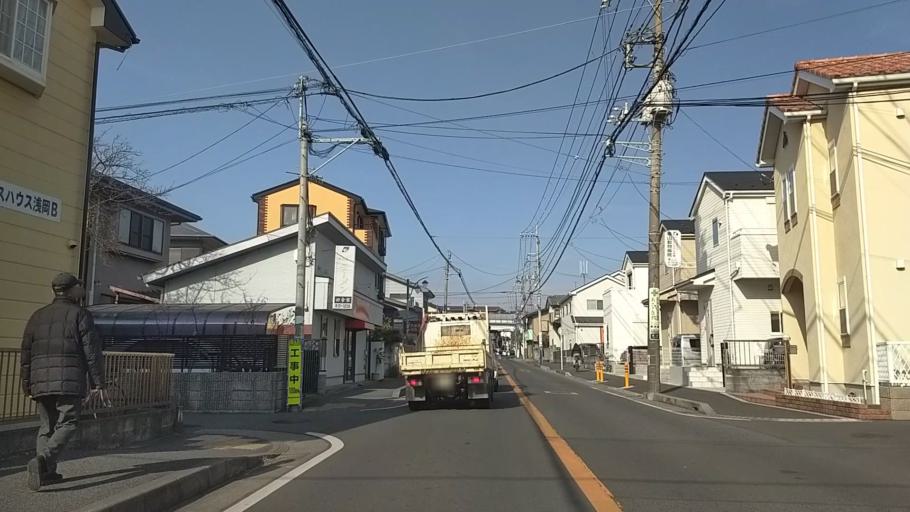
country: JP
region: Kanagawa
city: Chigasaki
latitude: 35.3480
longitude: 139.4137
